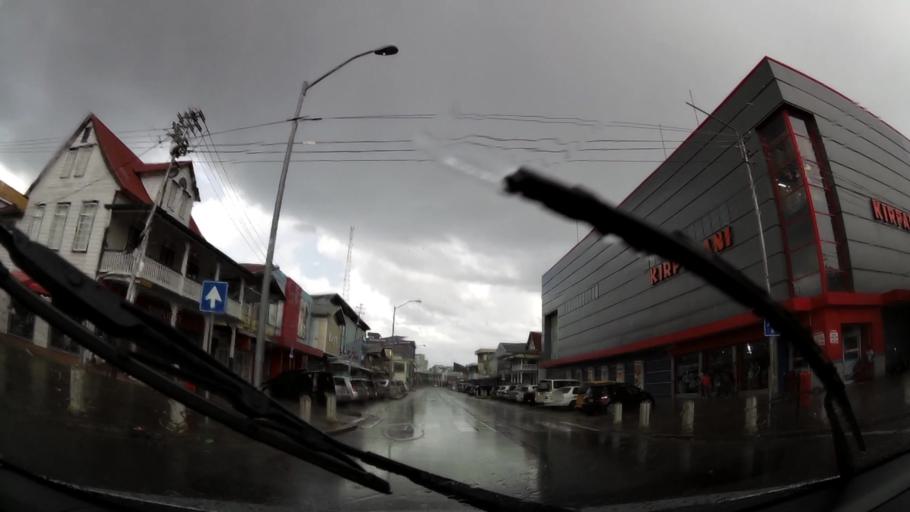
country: SR
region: Paramaribo
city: Paramaribo
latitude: 5.8254
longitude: -55.1587
